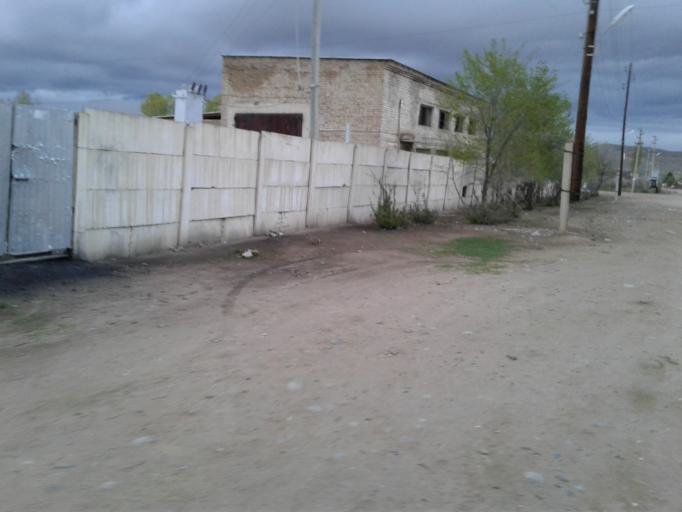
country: KG
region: Ysyk-Koel
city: Bokombayevskoye
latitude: 42.1183
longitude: 76.9881
